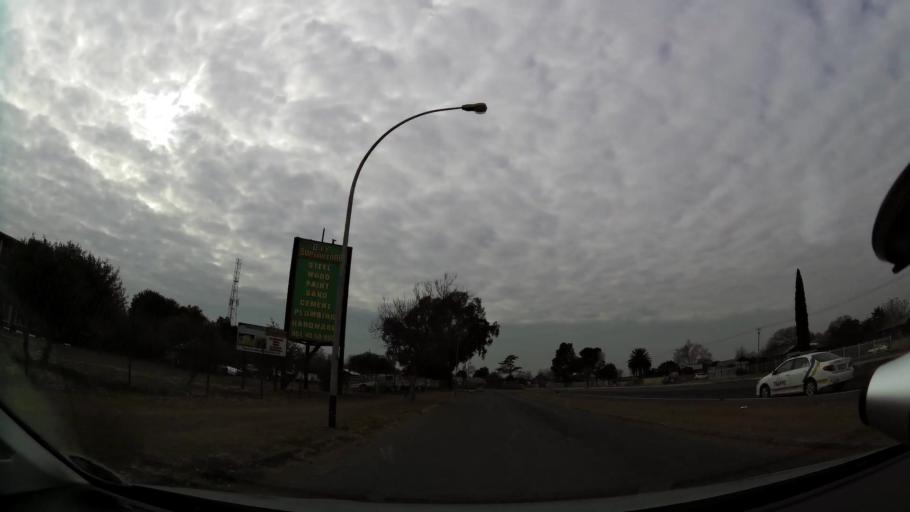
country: ZA
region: Orange Free State
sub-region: Mangaung Metropolitan Municipality
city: Bloemfontein
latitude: -29.1255
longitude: 26.1921
